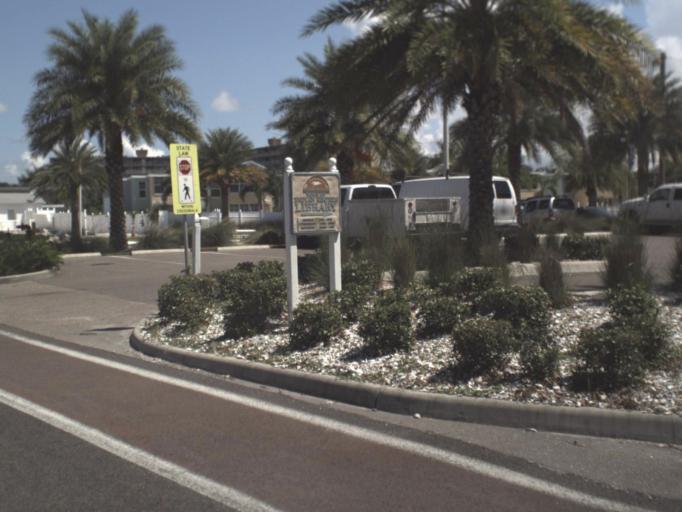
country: US
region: Florida
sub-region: Pinellas County
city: Indian Shores
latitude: 27.8480
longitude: -82.8432
